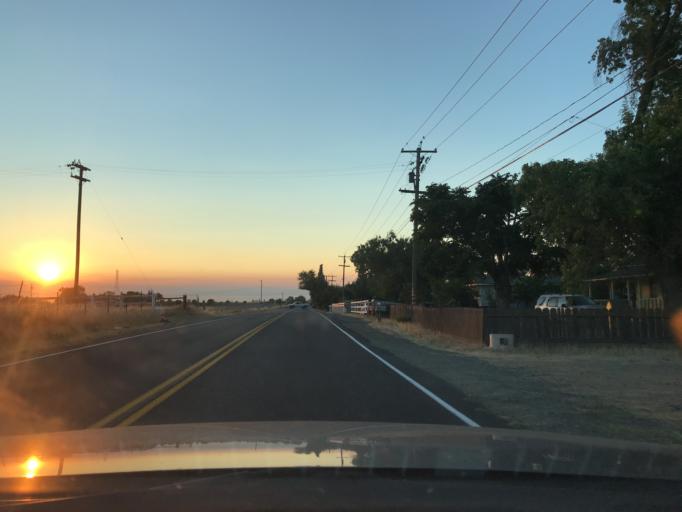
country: US
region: California
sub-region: Merced County
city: Merced
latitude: 37.3391
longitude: -120.5186
